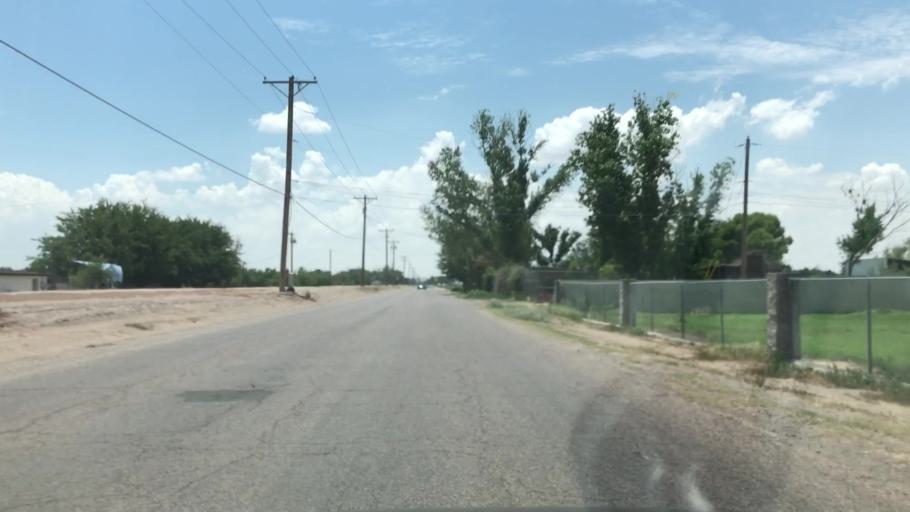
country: US
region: Texas
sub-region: El Paso County
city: Canutillo
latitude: 31.9147
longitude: -106.6249
